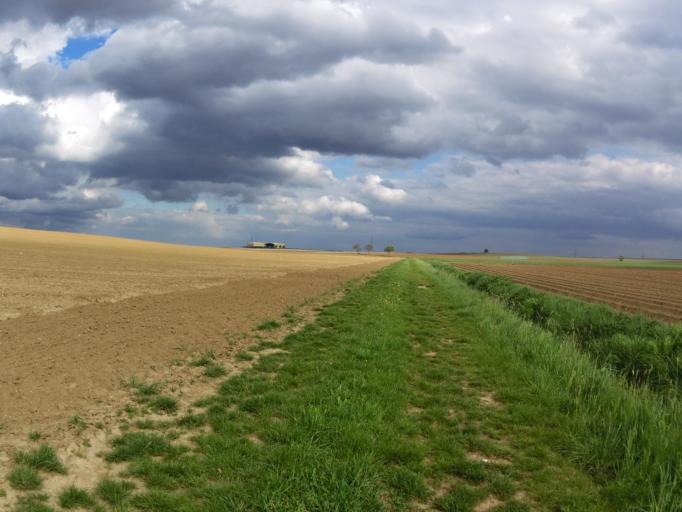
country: DE
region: Bavaria
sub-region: Regierungsbezirk Unterfranken
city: Oberpleichfeld
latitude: 49.8648
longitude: 10.0709
